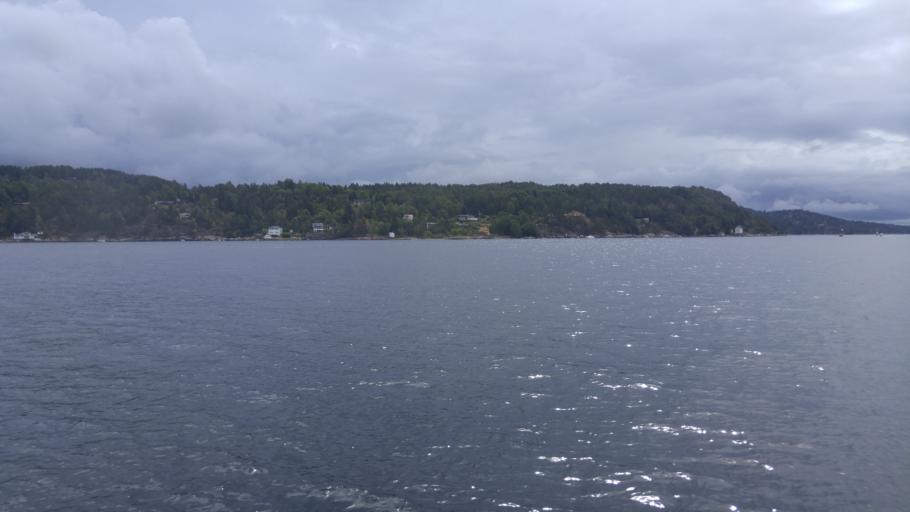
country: NO
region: Akershus
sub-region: Nesodden
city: Fagerstrand
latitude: 59.7270
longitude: 10.5779
